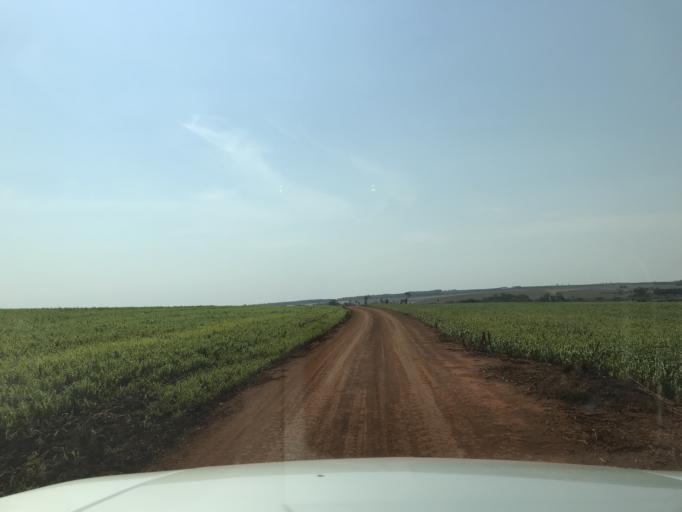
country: BR
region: Parana
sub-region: Palotina
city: Palotina
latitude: -24.2298
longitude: -53.7410
